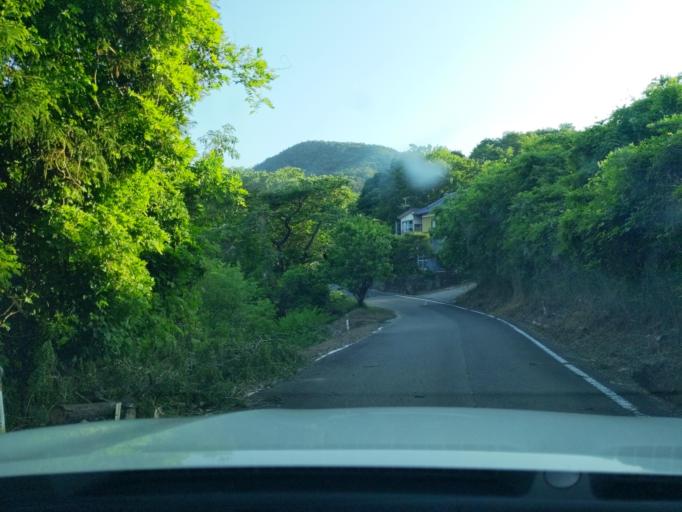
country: JP
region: Fukushima
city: Motomiya
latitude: 37.5251
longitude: 140.3547
